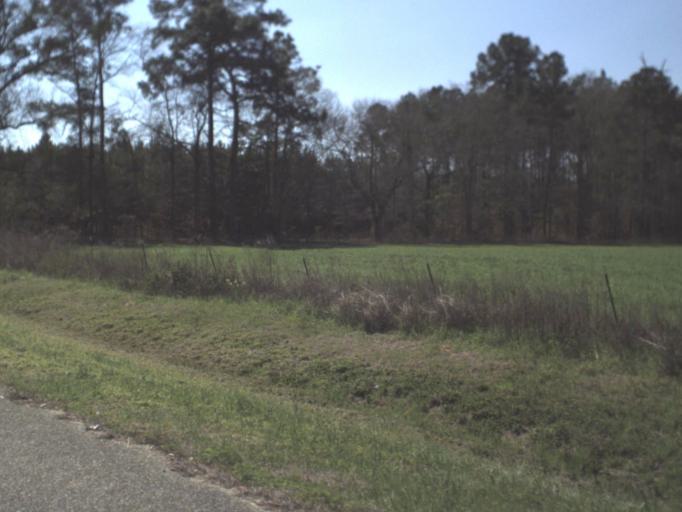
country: US
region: Florida
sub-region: Calhoun County
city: Blountstown
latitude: 30.5622
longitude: -85.0217
